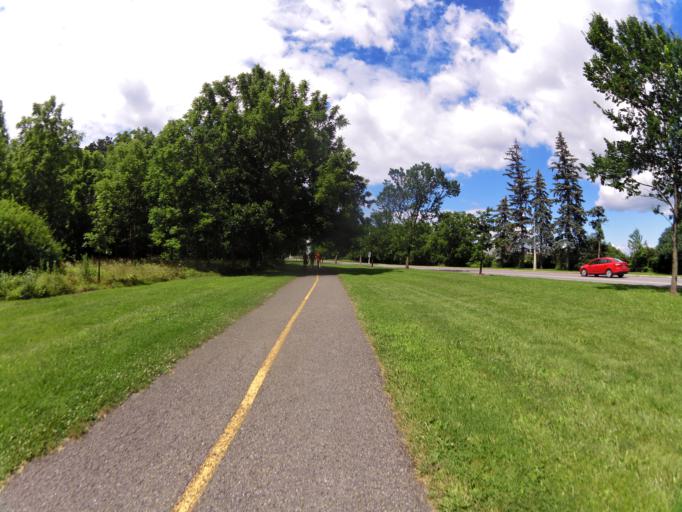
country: CA
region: Ontario
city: Ottawa
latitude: 45.3870
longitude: -75.7248
